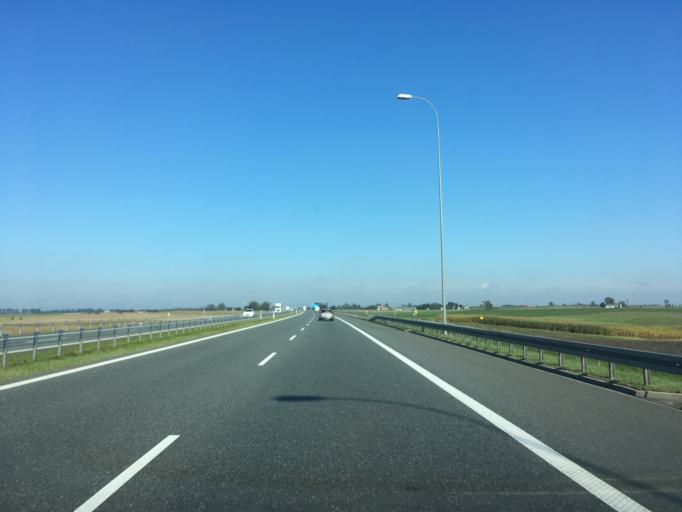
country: PL
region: Kujawsko-Pomorskie
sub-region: Powiat chelminski
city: Lisewo
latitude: 53.2653
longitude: 18.7218
